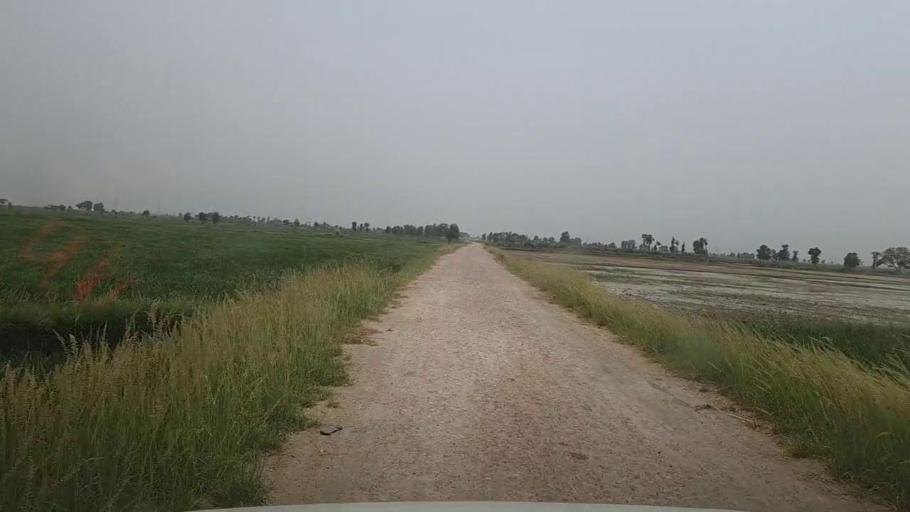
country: PK
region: Sindh
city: Sita Road
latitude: 27.0609
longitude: 67.8563
